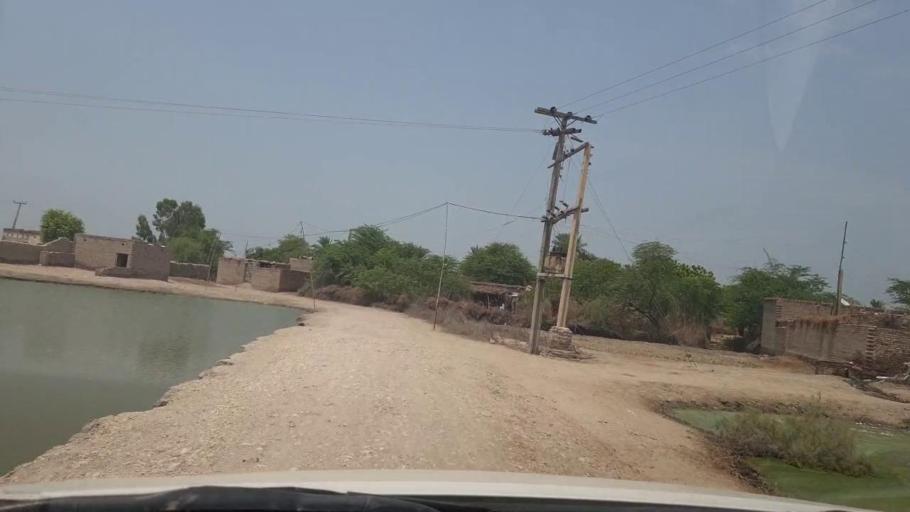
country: PK
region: Sindh
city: Rustam jo Goth
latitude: 28.0420
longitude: 68.7532
